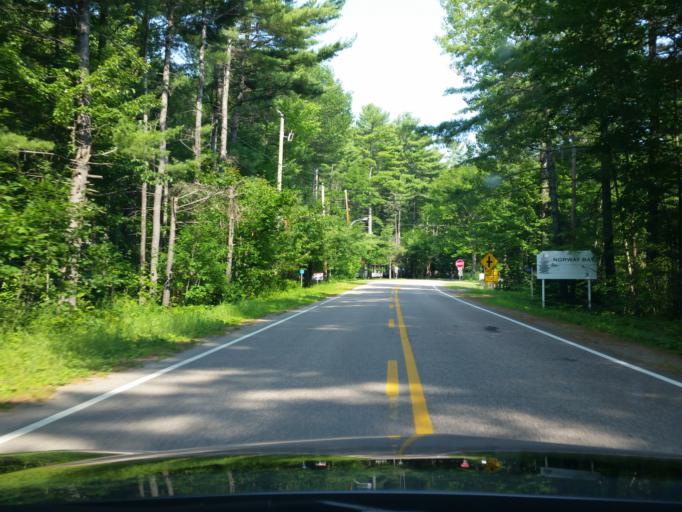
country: CA
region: Quebec
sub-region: Outaouais
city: Shawville
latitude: 45.5210
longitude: -76.4282
